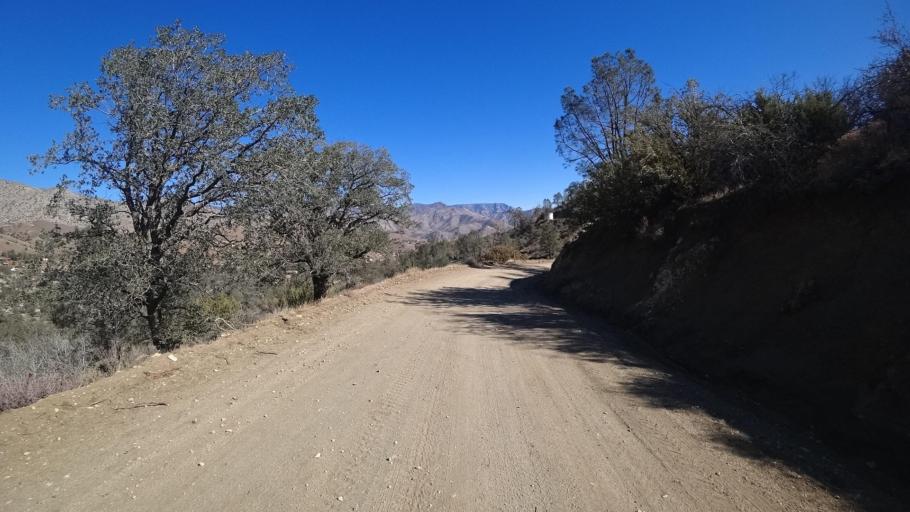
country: US
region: California
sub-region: Kern County
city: Wofford Heights
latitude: 35.7051
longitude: -118.4782
